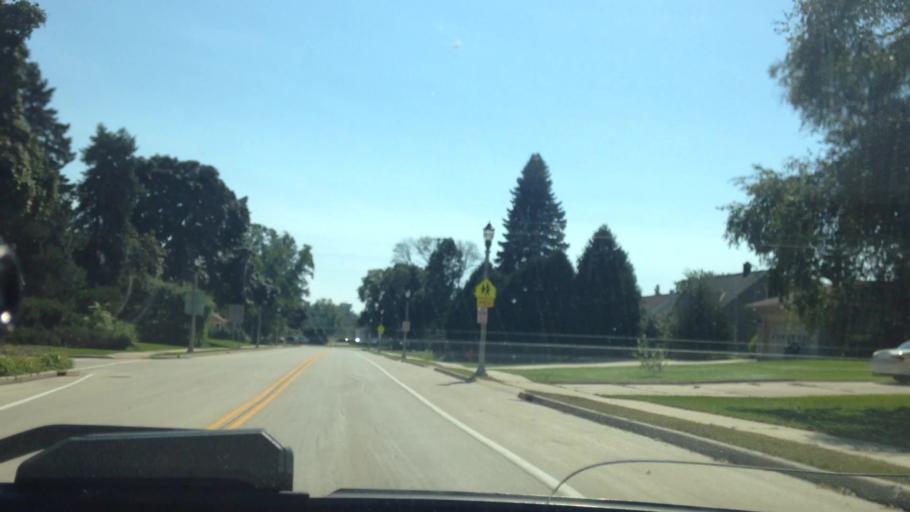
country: US
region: Wisconsin
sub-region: Ozaukee County
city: Port Washington
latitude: 43.3863
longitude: -87.8858
